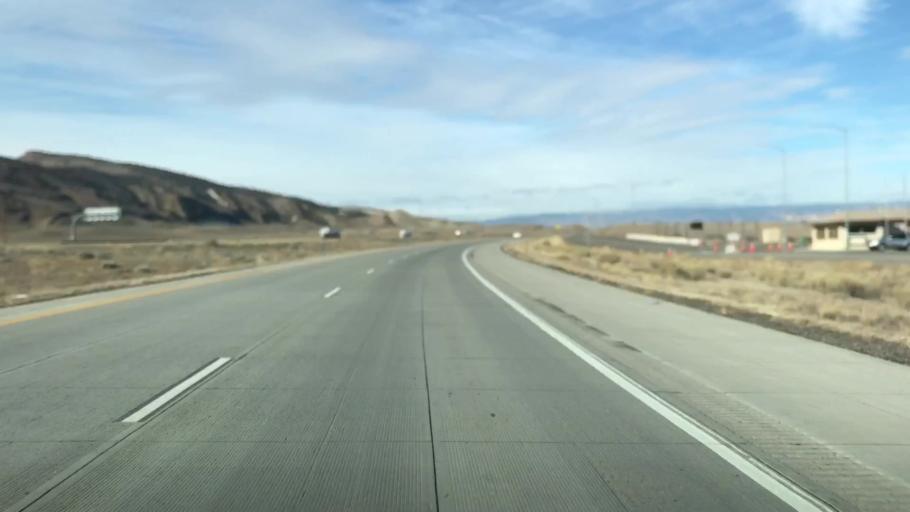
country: US
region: Colorado
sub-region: Mesa County
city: Loma
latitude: 39.1801
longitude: -108.8246
